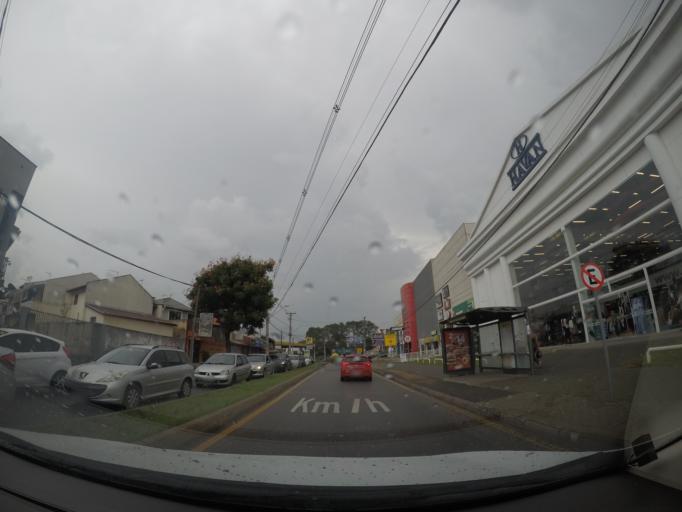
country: BR
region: Parana
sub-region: Sao Jose Dos Pinhais
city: Sao Jose dos Pinhais
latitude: -25.5180
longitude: -49.2555
